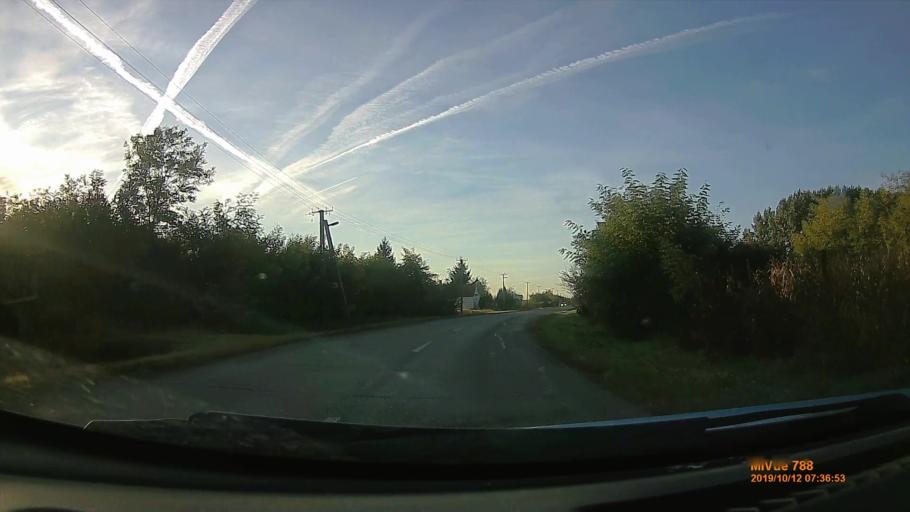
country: HU
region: Hajdu-Bihar
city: Pocsaj
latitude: 47.2420
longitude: 21.8148
